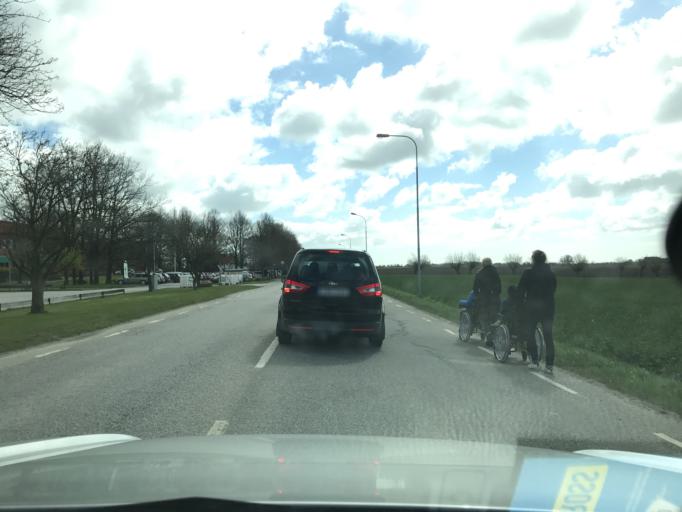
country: SE
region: Skane
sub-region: Skurups Kommun
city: Skurup
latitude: 55.4702
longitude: 13.5186
